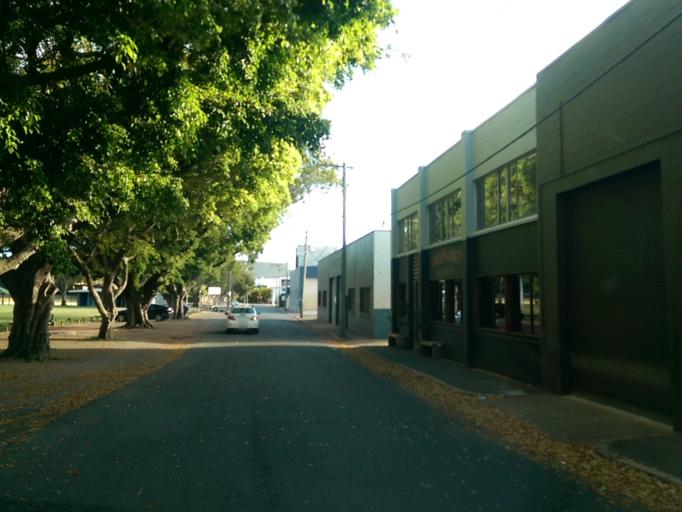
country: AU
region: Queensland
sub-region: Brisbane
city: Wooloowin
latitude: -27.4325
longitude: 153.0454
